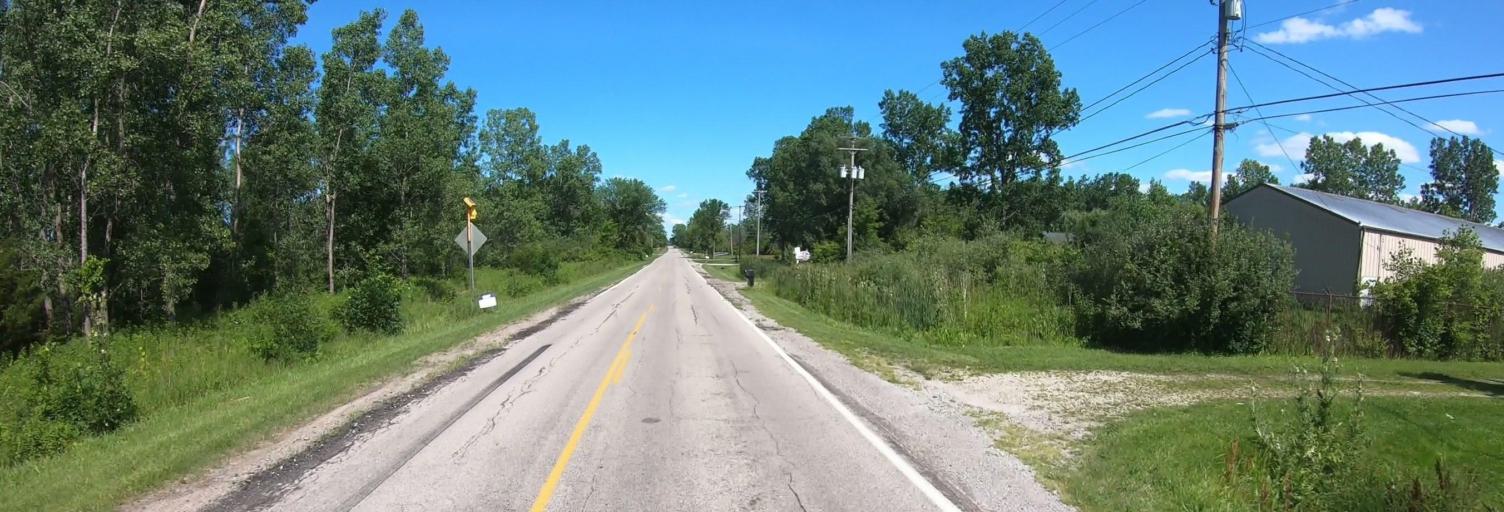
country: US
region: Michigan
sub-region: Genesee County
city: Flushing
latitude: 43.0783
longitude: -83.8098
